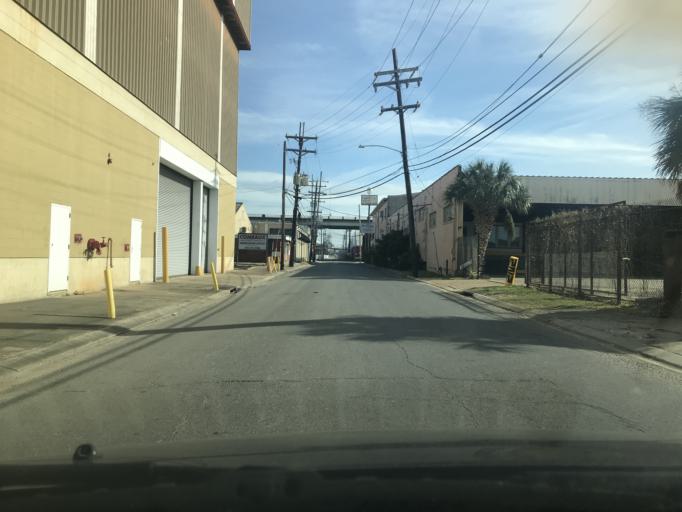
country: US
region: Louisiana
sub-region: Orleans Parish
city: New Orleans
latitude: 29.9566
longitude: -90.0969
